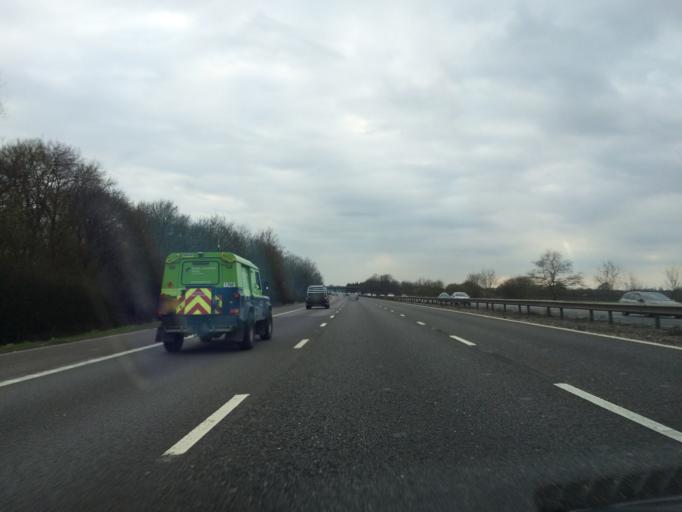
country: GB
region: England
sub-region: Bracknell Forest
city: Binfield
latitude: 51.4494
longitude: -0.8133
